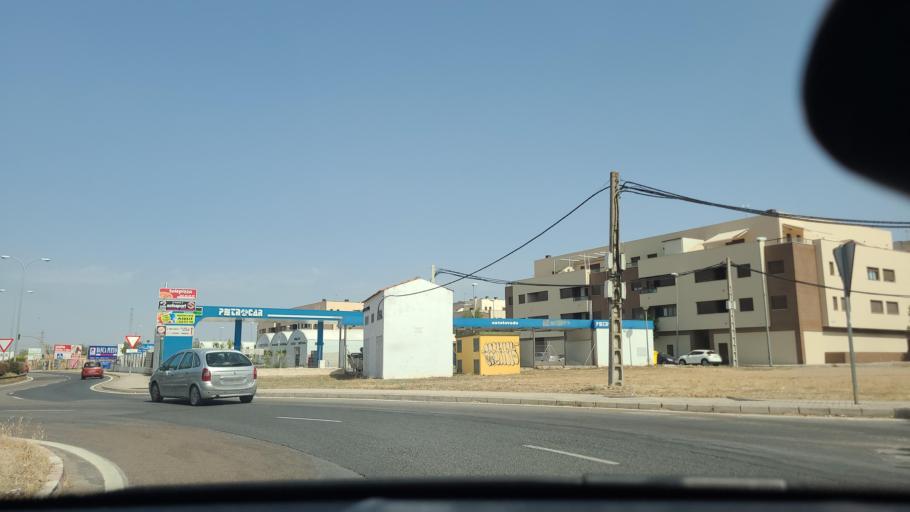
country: ES
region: Extremadura
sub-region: Provincia de Badajoz
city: Zafra
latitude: 38.4294
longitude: -6.4128
